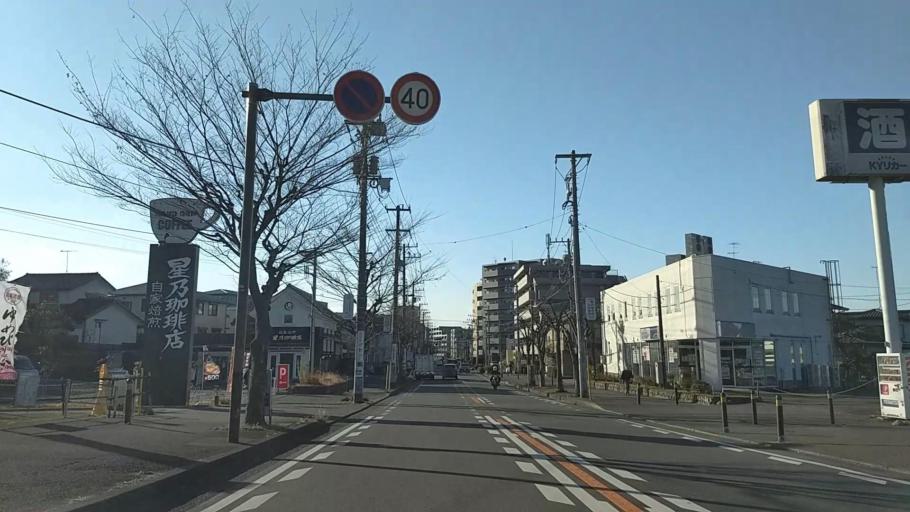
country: JP
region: Kanagawa
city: Fujisawa
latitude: 35.3221
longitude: 139.4863
